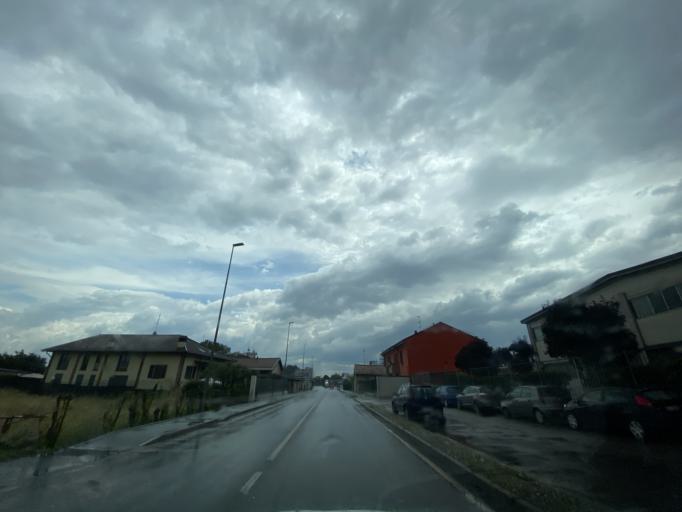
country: IT
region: Lombardy
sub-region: Citta metropolitana di Milano
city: Novate Milanese
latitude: 45.5235
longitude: 9.1497
